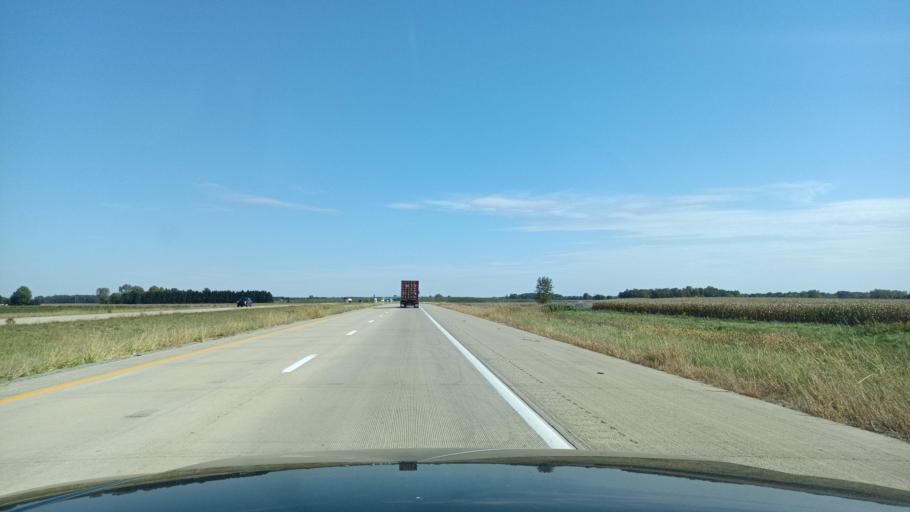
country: US
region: Ohio
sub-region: Henry County
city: Liberty Center
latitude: 41.4332
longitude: -83.9341
